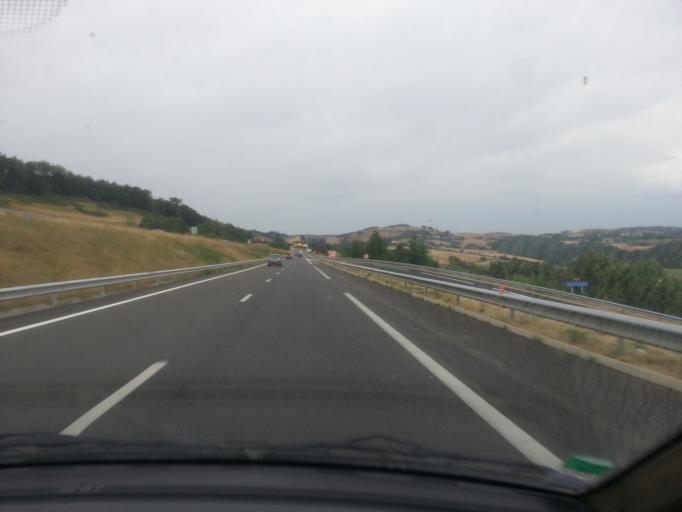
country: FR
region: Languedoc-Roussillon
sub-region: Departement de la Lozere
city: Marvejols
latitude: 44.5584
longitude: 3.2549
